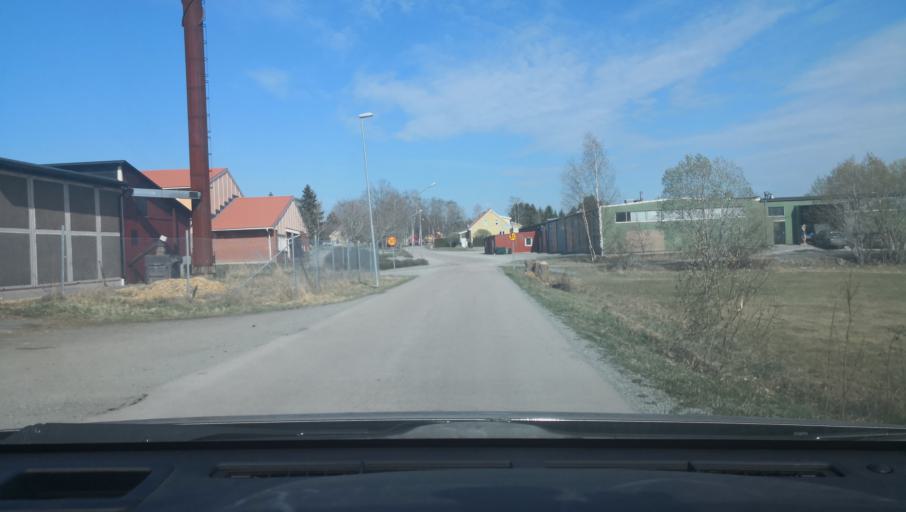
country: SE
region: Uppsala
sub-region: Enkopings Kommun
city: Irsta
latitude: 59.7734
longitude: 16.9244
